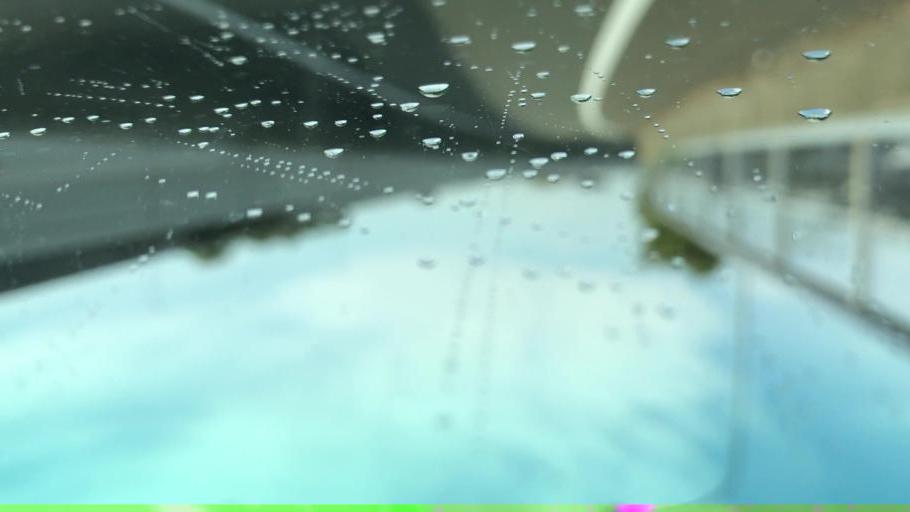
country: JP
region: Hokkaido
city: Sapporo
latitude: 43.0903
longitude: 141.2667
